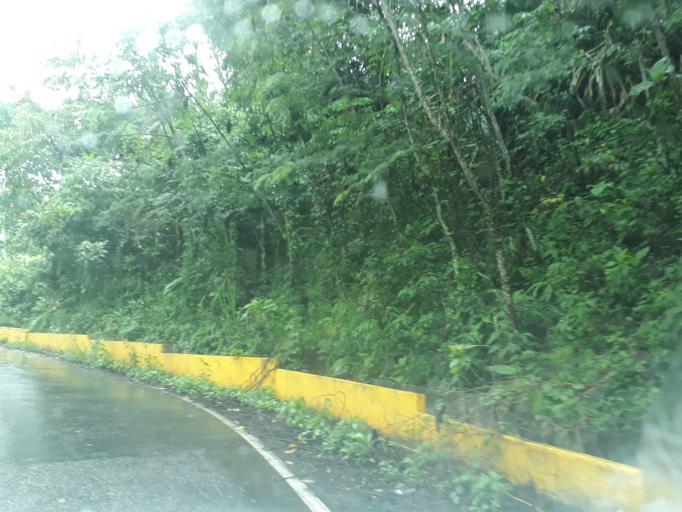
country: CO
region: Cundinamarca
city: Paratebueno
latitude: 4.4003
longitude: -73.3057
